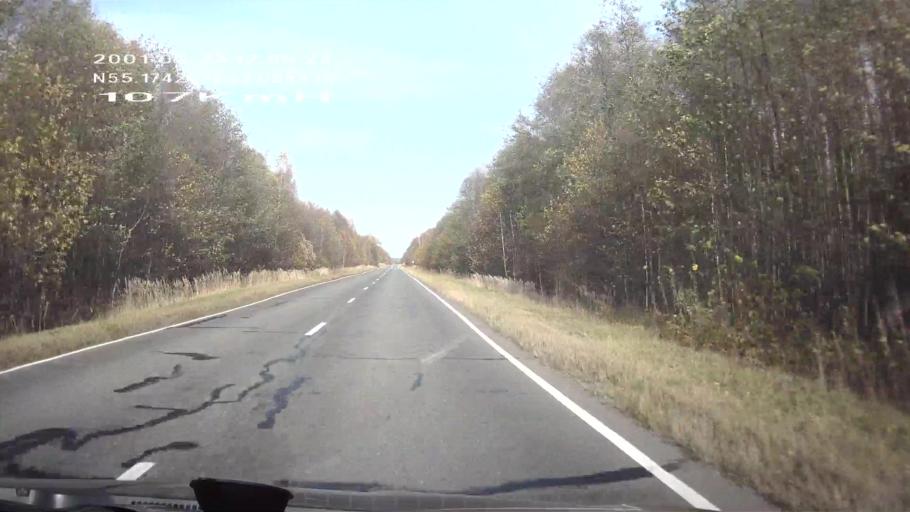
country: RU
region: Chuvashia
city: Buinsk
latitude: 55.1747
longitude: 47.0592
